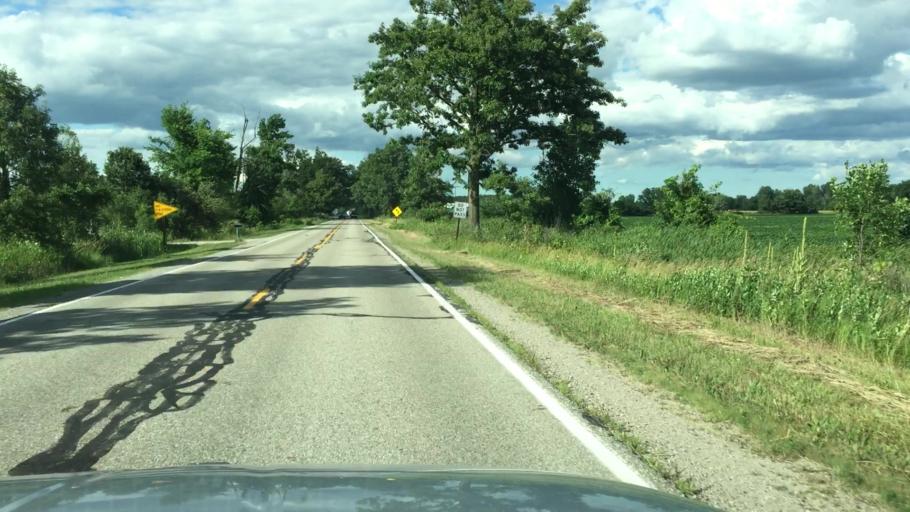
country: US
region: Michigan
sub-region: Saint Clair County
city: Capac
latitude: 43.0888
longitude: -82.9111
